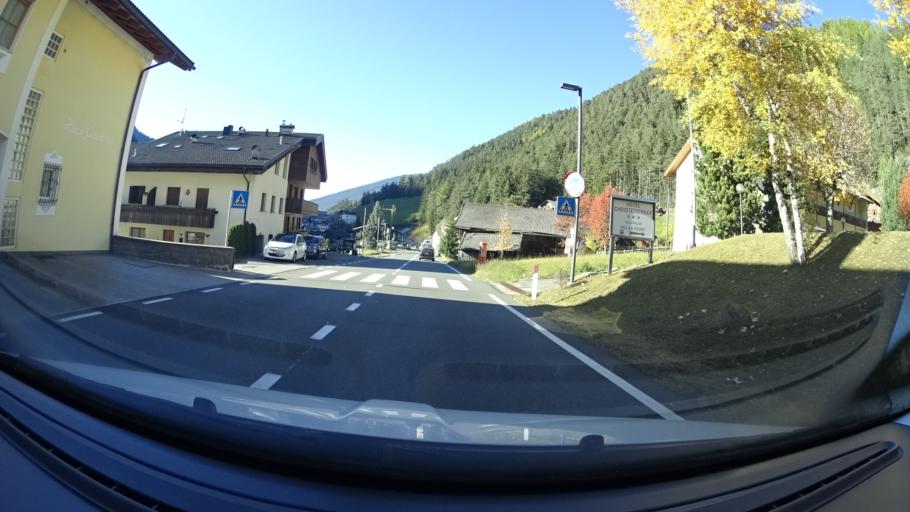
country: IT
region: Trentino-Alto Adige
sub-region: Bolzano
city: Santa Cristina Valgardena
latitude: 46.5596
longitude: 11.7091
